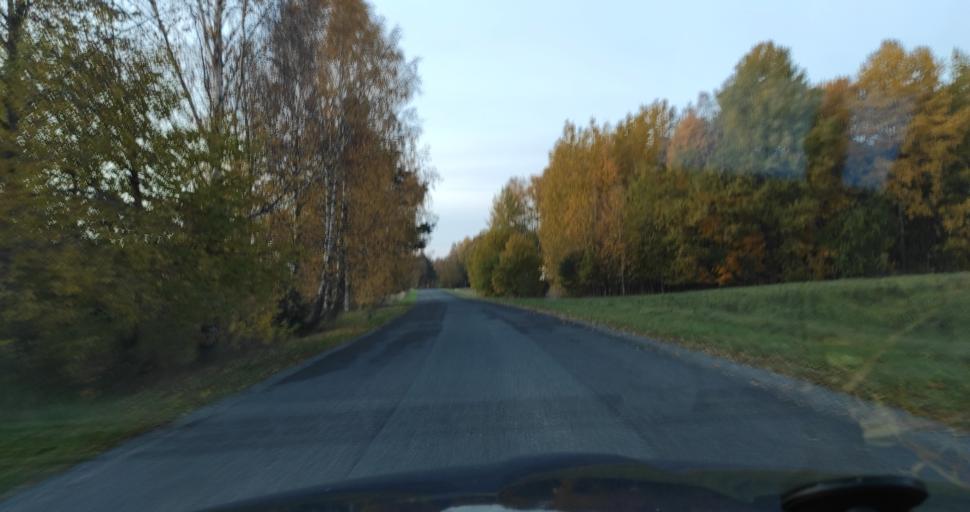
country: LV
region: Aizpute
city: Aizpute
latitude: 56.7086
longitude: 21.7923
